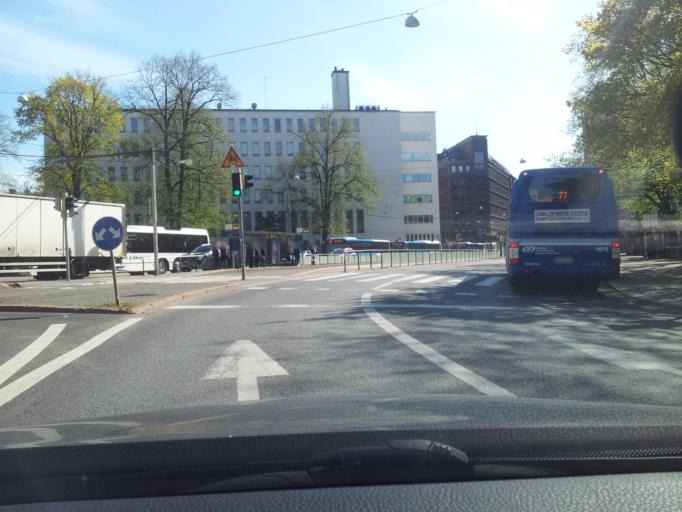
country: FI
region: Uusimaa
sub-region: Helsinki
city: Helsinki
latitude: 60.1740
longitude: 24.9497
